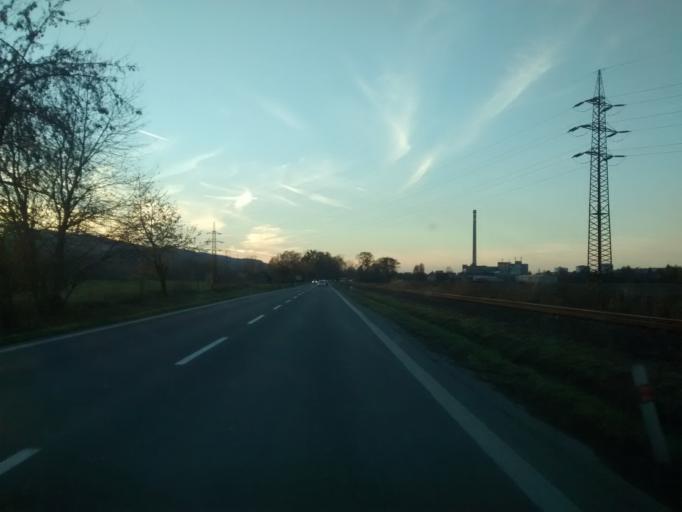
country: CZ
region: Zlin
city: Zubri
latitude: 49.4602
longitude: 18.1032
